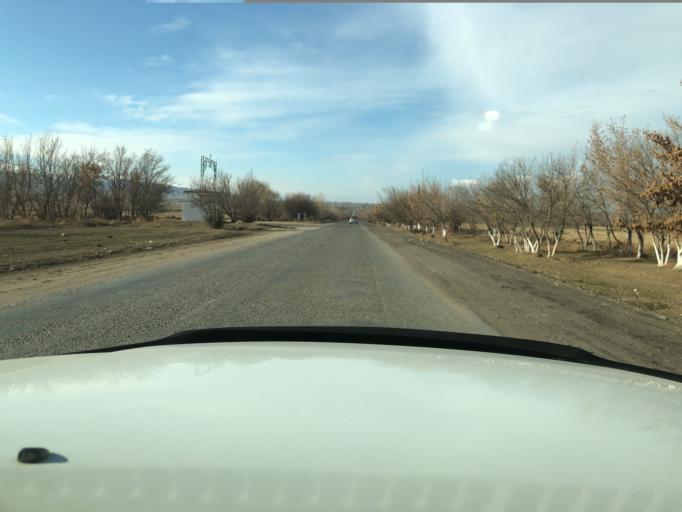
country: KG
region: Ysyk-Koel
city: Pokrovka
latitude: 42.3309
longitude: 77.9719
